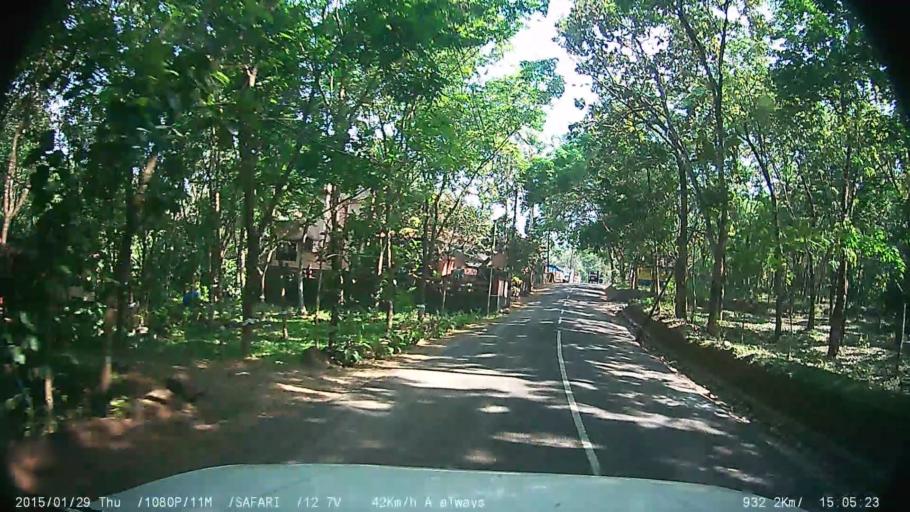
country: IN
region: Kerala
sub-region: Kottayam
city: Palackattumala
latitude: 9.7243
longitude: 76.5941
